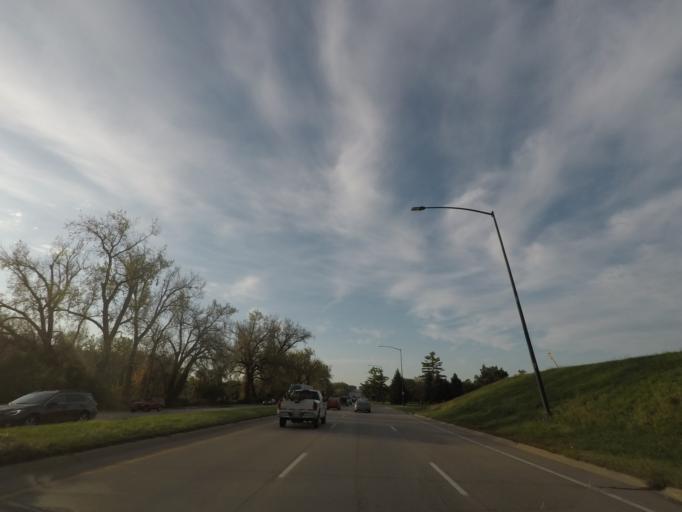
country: US
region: Iowa
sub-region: Polk County
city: Des Moines
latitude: 41.5770
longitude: -93.6450
